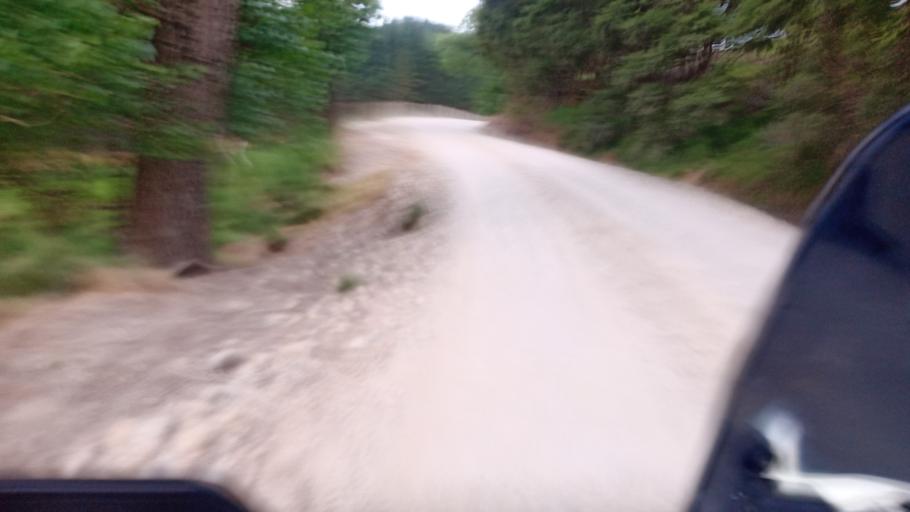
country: NZ
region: Gisborne
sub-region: Gisborne District
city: Gisborne
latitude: -38.4828
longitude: 177.9604
